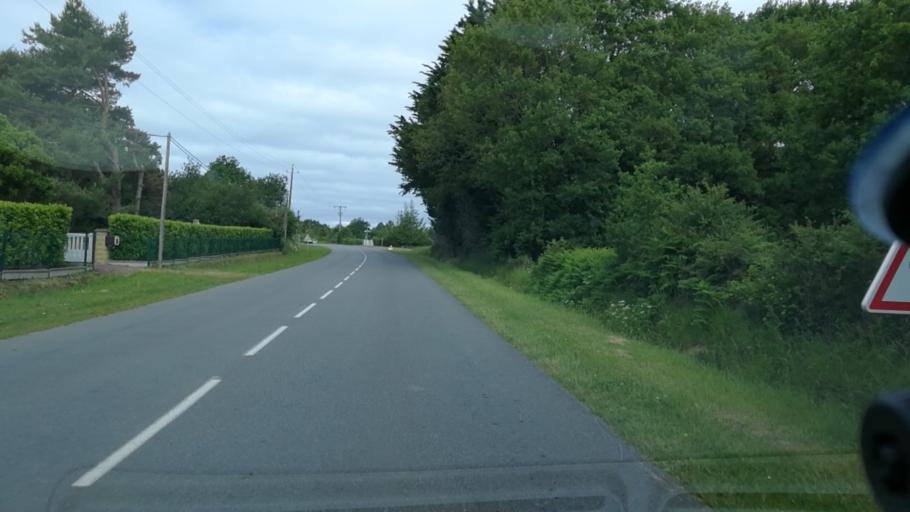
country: FR
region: Brittany
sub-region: Departement du Morbihan
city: Penestin
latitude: 47.4547
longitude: -2.4647
